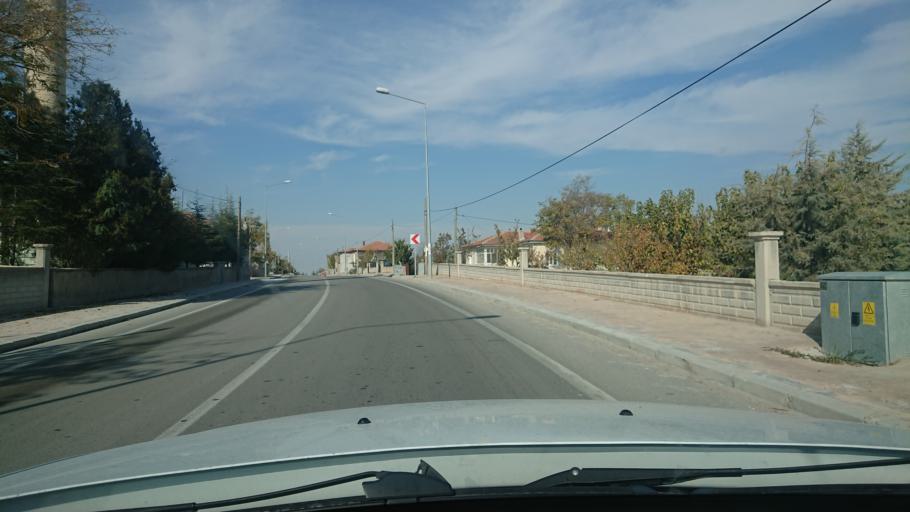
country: TR
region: Aksaray
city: Sultanhani
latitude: 38.2518
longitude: 33.4495
